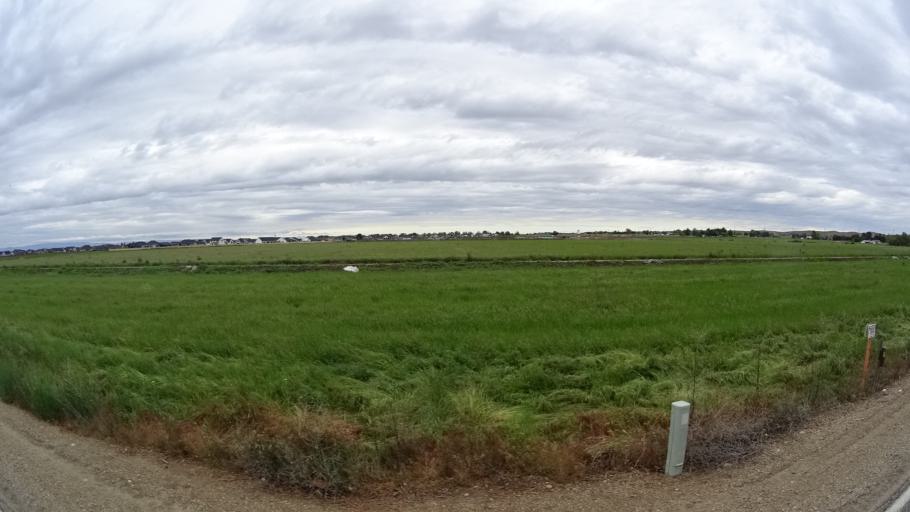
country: US
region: Idaho
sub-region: Ada County
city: Eagle
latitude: 43.7150
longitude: -116.4135
